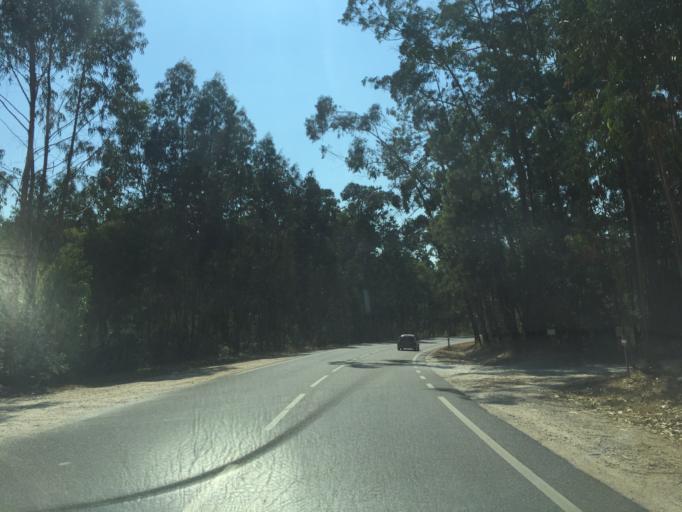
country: PT
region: Coimbra
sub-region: Cantanhede
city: Cantanhede
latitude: 40.3566
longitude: -8.5302
